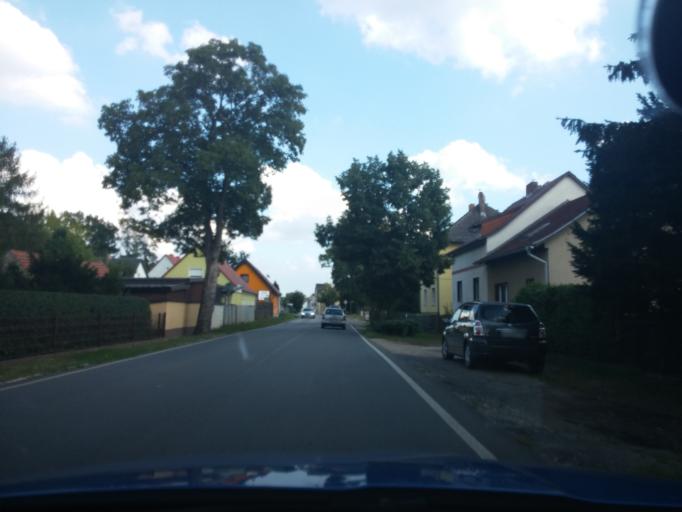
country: DE
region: Brandenburg
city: Halbe
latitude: 52.1075
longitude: 13.6938
